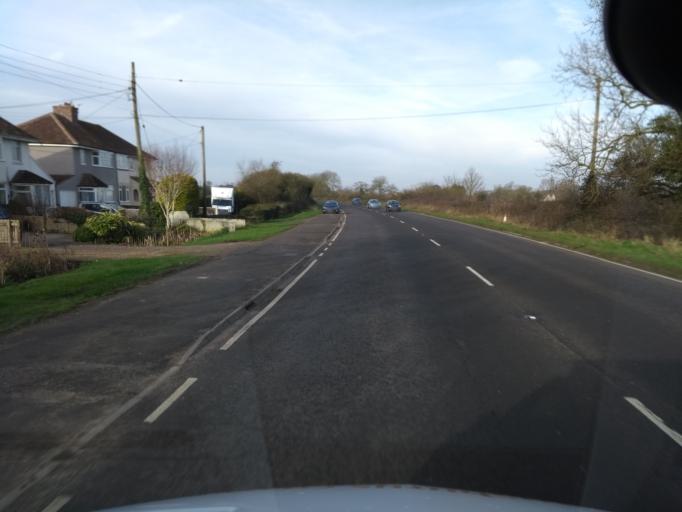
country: GB
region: England
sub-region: North Somerset
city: Bleadon
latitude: 51.2821
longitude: -2.9370
